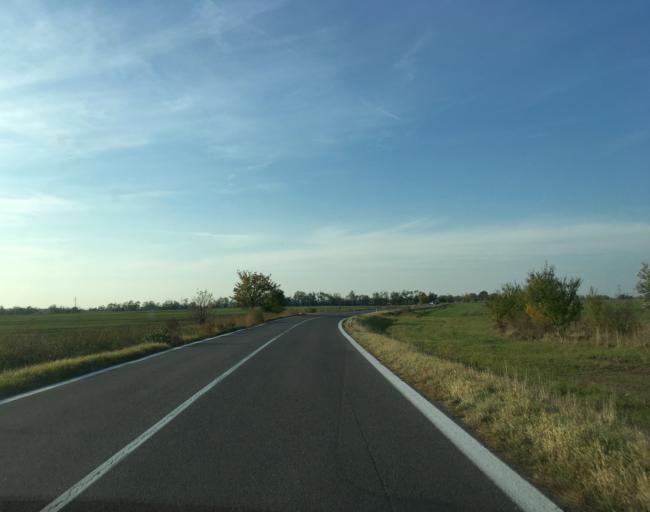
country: SK
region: Nitriansky
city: Surany
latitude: 48.0532
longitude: 18.1096
